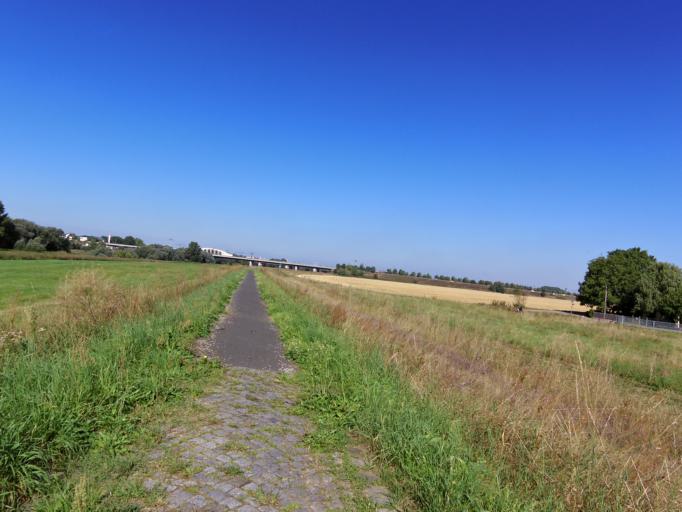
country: DE
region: Saxony
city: Riesa
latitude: 51.3087
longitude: 13.3061
